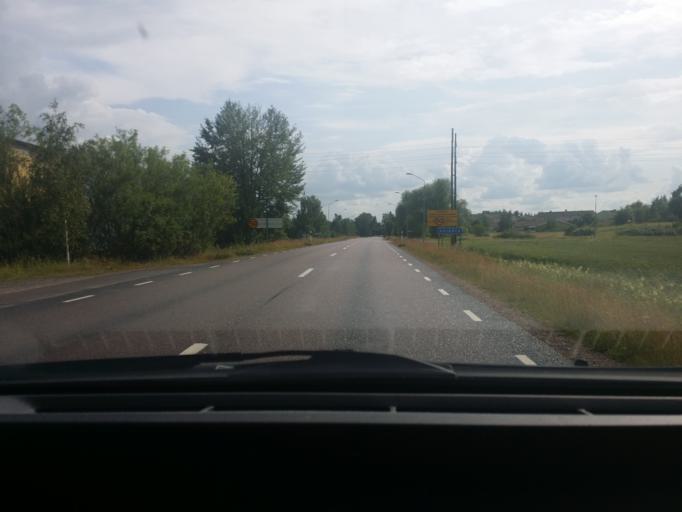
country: SE
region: Vaestmanland
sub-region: Hallstahammars Kommun
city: Kolback
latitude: 59.5707
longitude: 16.2389
